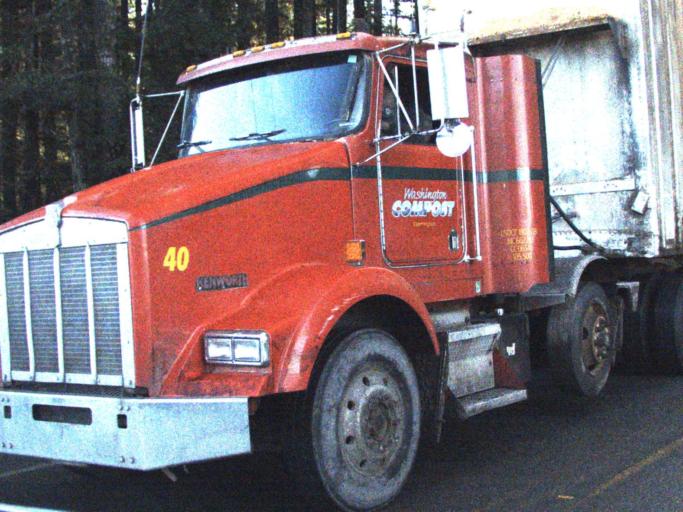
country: US
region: Washington
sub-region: Snohomish County
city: Darrington
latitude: 48.2626
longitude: -121.6018
